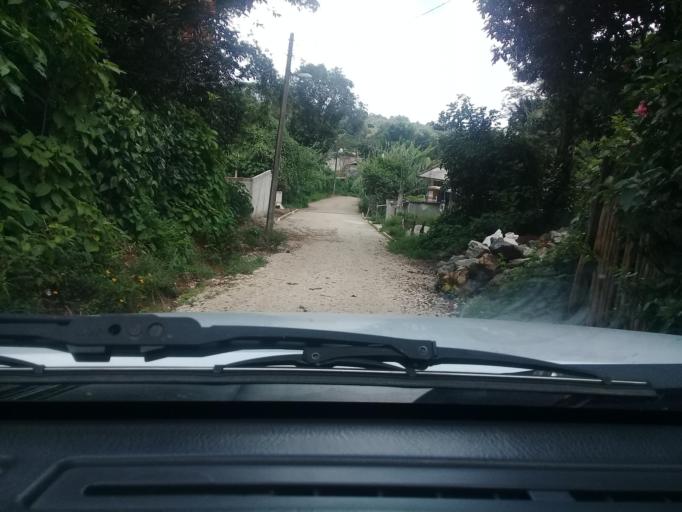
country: MX
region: Veracruz
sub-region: Tlalnelhuayocan
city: Otilpan
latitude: 19.5402
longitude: -96.9777
